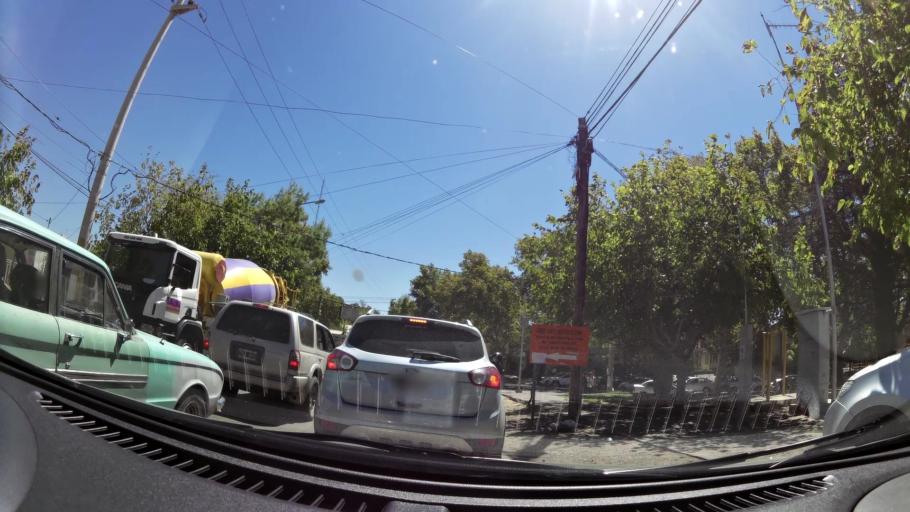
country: AR
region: San Juan
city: San Juan
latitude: -31.5314
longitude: -68.5537
